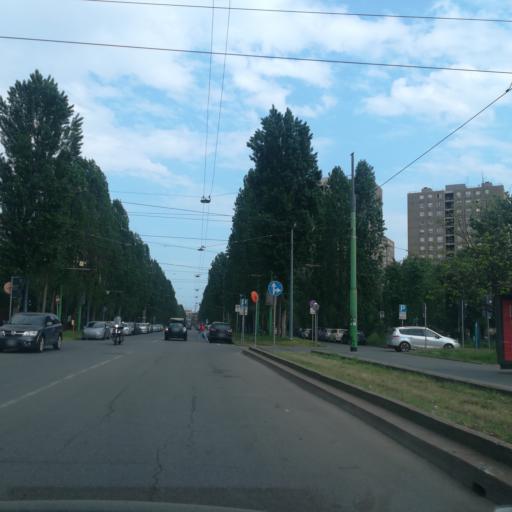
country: IT
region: Lombardy
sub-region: Citta metropolitana di Milano
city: Bresso
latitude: 45.5088
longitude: 9.1904
